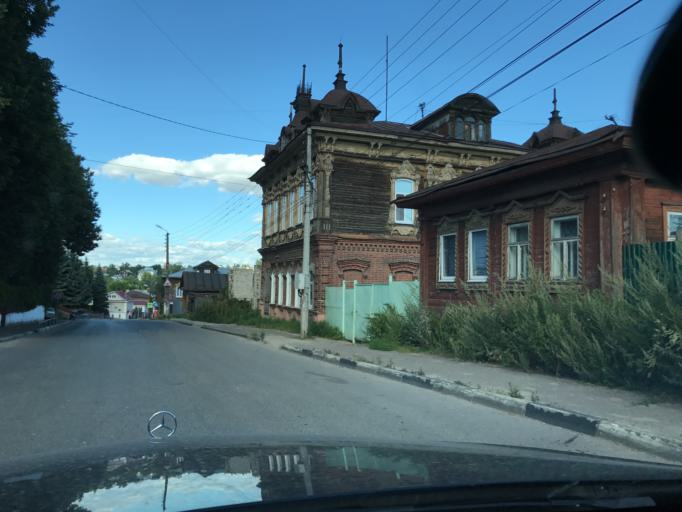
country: RU
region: Nizjnij Novgorod
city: Pavlovo
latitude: 55.9617
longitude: 43.0645
